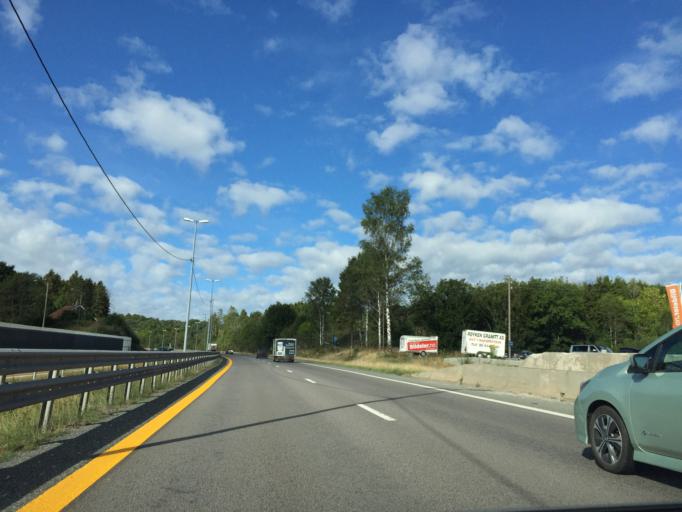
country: NO
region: Buskerud
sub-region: Lier
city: Tranby
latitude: 59.8185
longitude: 10.3261
